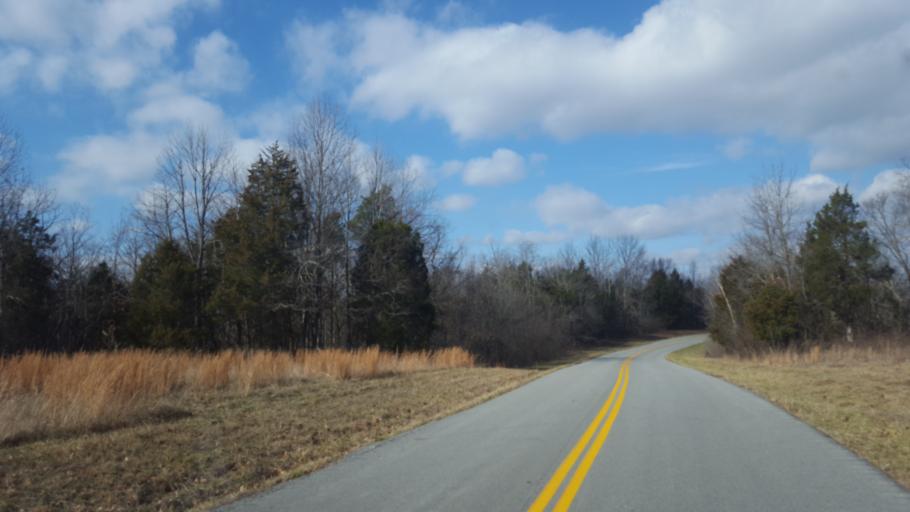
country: US
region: Kentucky
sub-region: Franklin County
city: Frankfort
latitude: 38.3753
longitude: -84.9471
